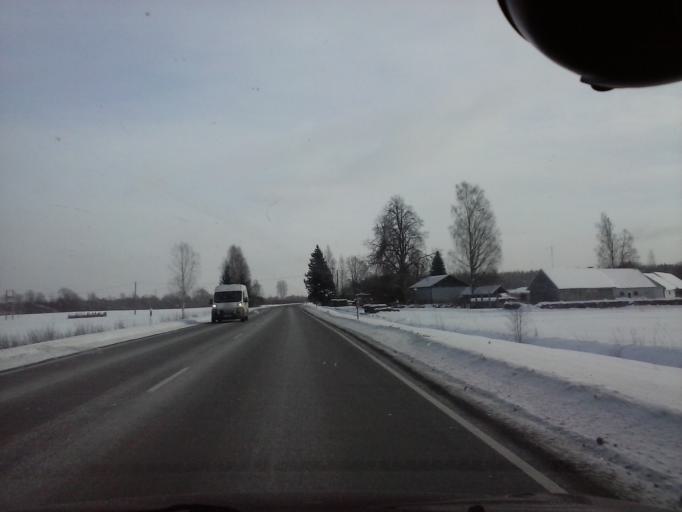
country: EE
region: Paernumaa
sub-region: Paikuse vald
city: Paikuse
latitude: 58.2018
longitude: 24.7303
